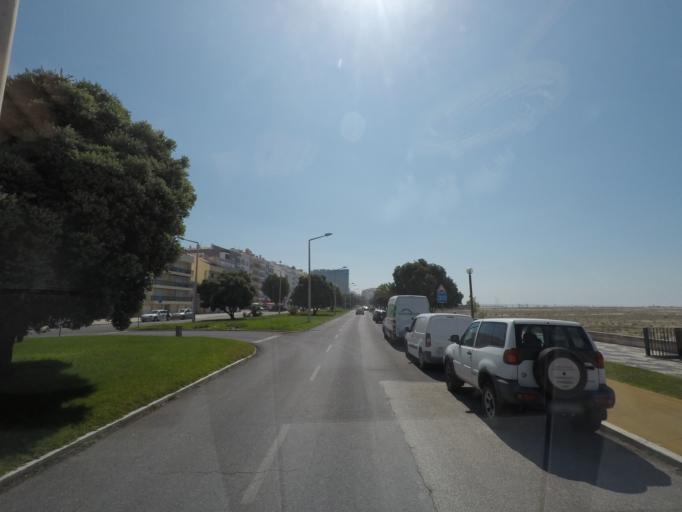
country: PT
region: Coimbra
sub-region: Figueira da Foz
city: Buarcos
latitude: 40.1598
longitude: -8.8704
